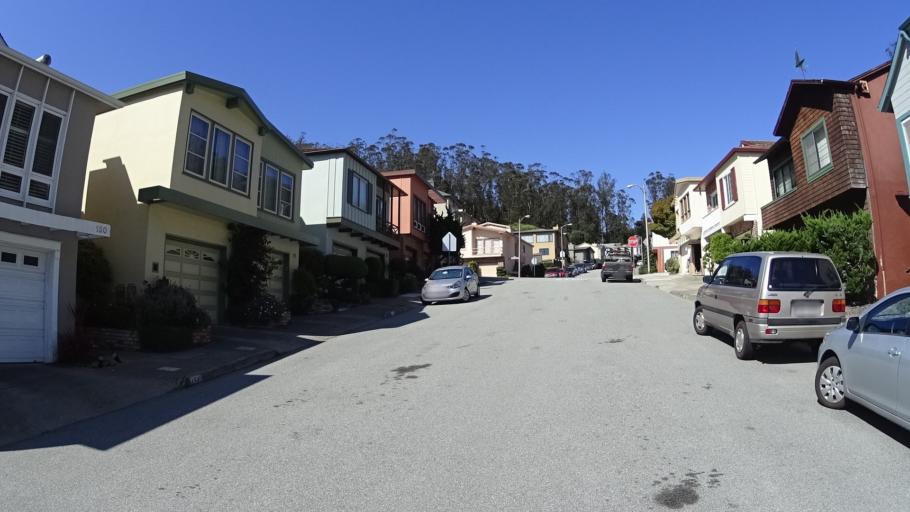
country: US
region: California
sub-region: San Francisco County
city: San Francisco
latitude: 37.7548
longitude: -122.4557
